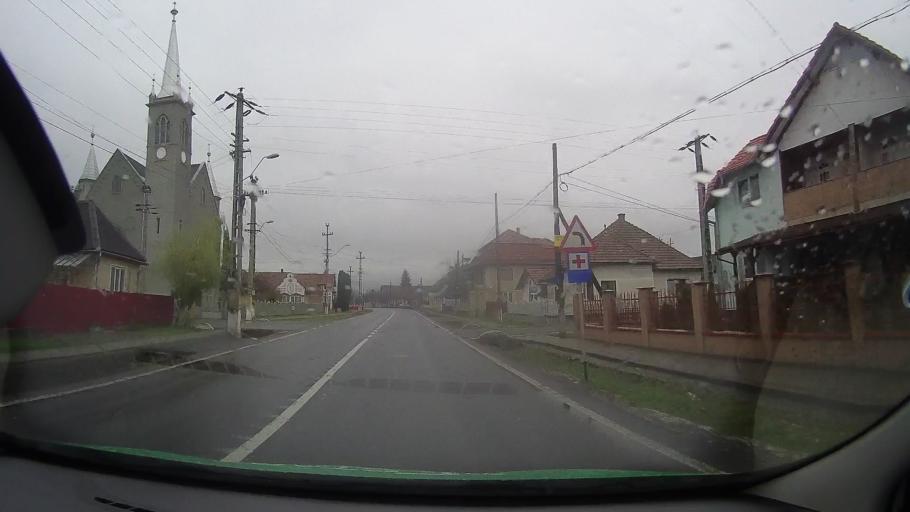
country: RO
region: Mures
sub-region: Comuna Suseni
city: Suseni
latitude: 46.8143
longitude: 24.7324
